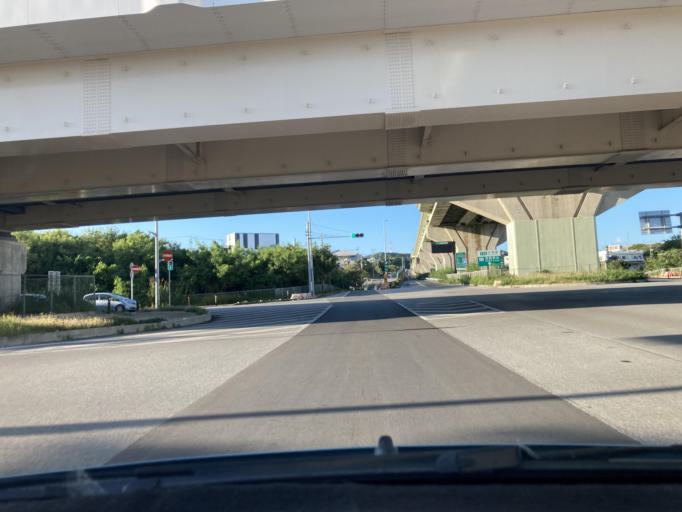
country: JP
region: Okinawa
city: Naha-shi
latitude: 26.2021
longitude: 127.7389
